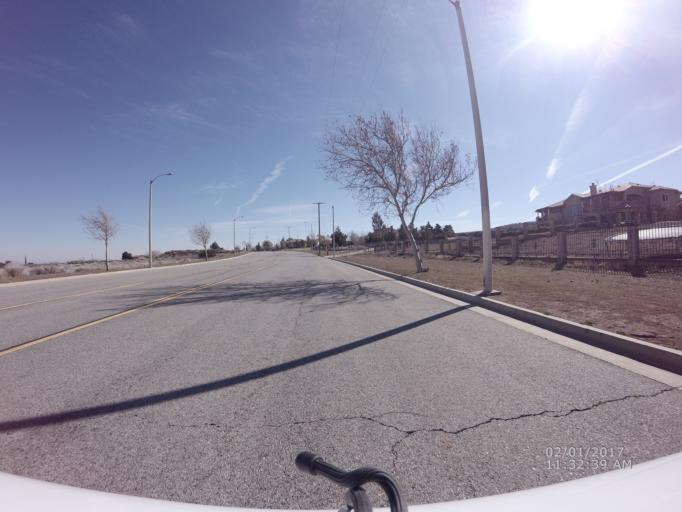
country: US
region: California
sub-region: Los Angeles County
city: Palmdale
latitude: 34.5427
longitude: -118.1184
